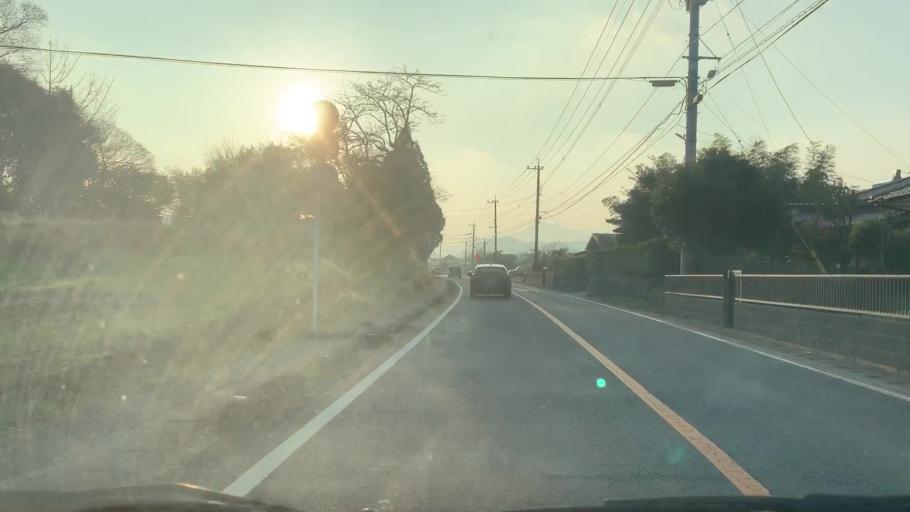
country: JP
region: Saga Prefecture
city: Takeocho-takeo
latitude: 33.2690
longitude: 130.1039
